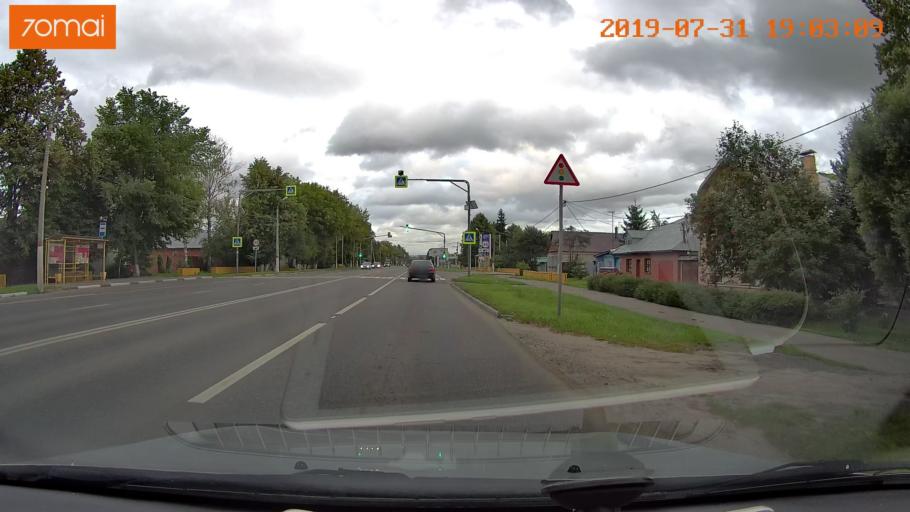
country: RU
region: Moskovskaya
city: Raduzhnyy
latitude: 55.1166
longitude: 38.7363
